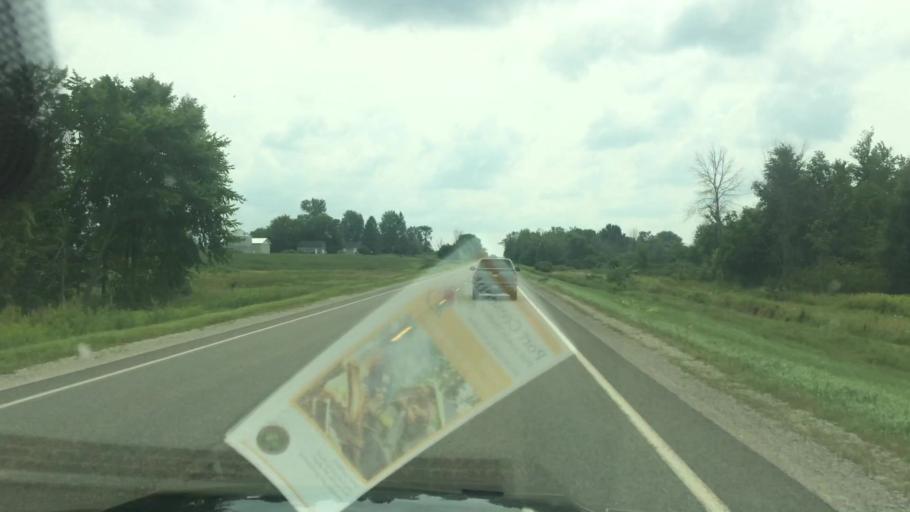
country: US
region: Michigan
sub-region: Tuscola County
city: Cass City
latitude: 43.6842
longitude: -83.0982
